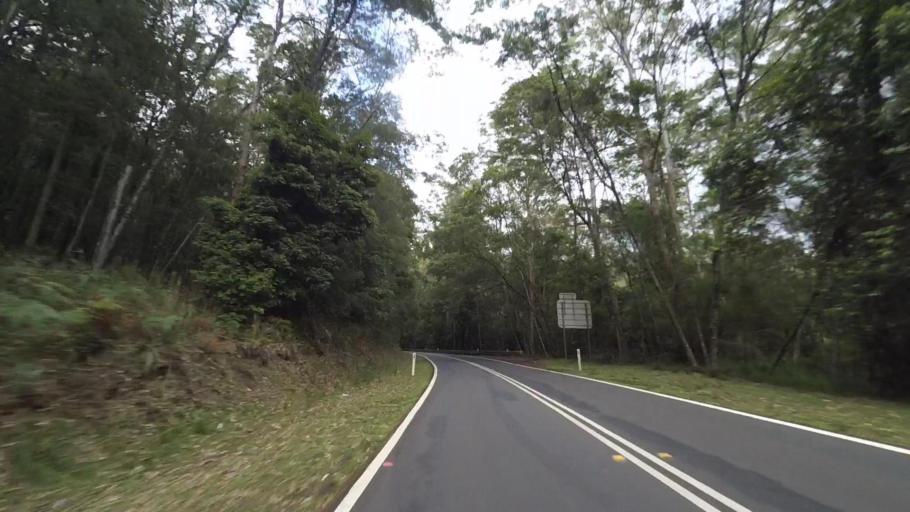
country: AU
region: New South Wales
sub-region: Wollongong
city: Helensburgh
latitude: -34.1536
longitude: 151.0291
